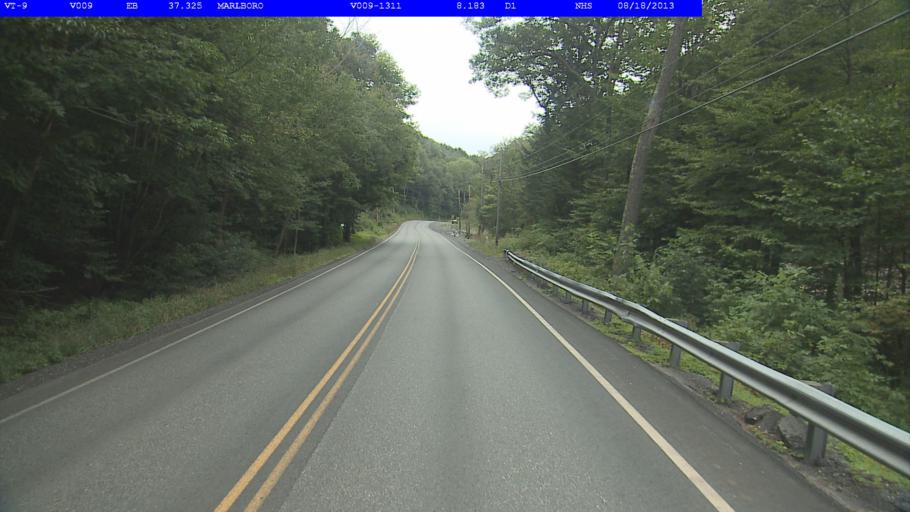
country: US
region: Vermont
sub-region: Windham County
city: West Brattleboro
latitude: 42.8774
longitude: -72.6805
